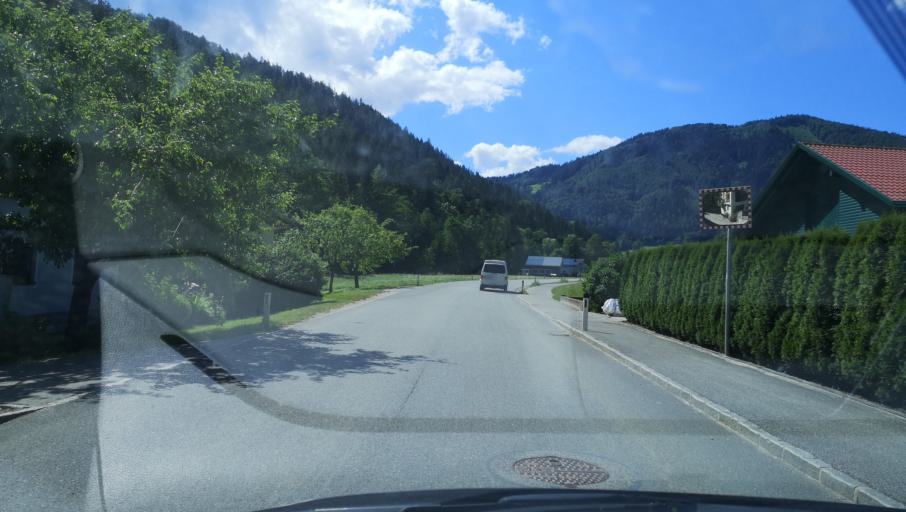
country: AT
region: Lower Austria
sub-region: Politischer Bezirk Scheibbs
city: Gresten
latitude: 47.9387
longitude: 15.0280
